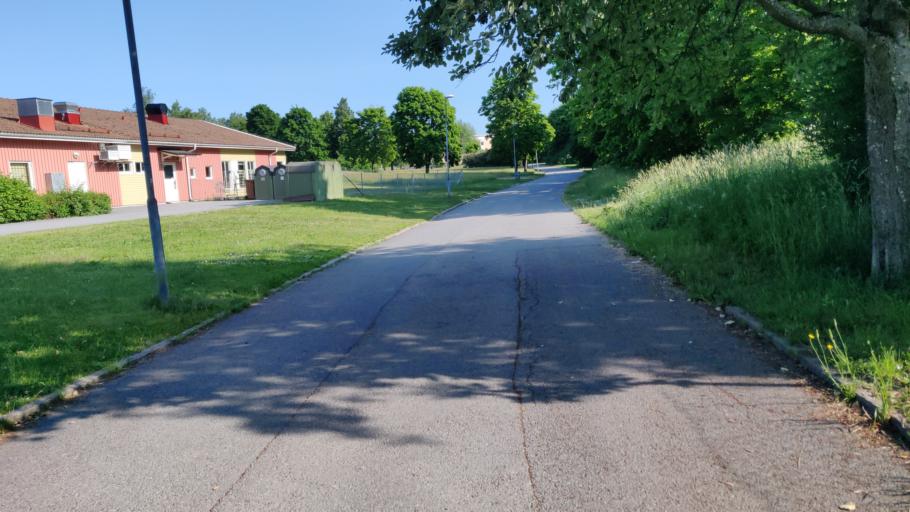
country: SE
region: OErebro
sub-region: Orebro Kommun
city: Orebro
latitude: 59.2905
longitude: 15.1680
